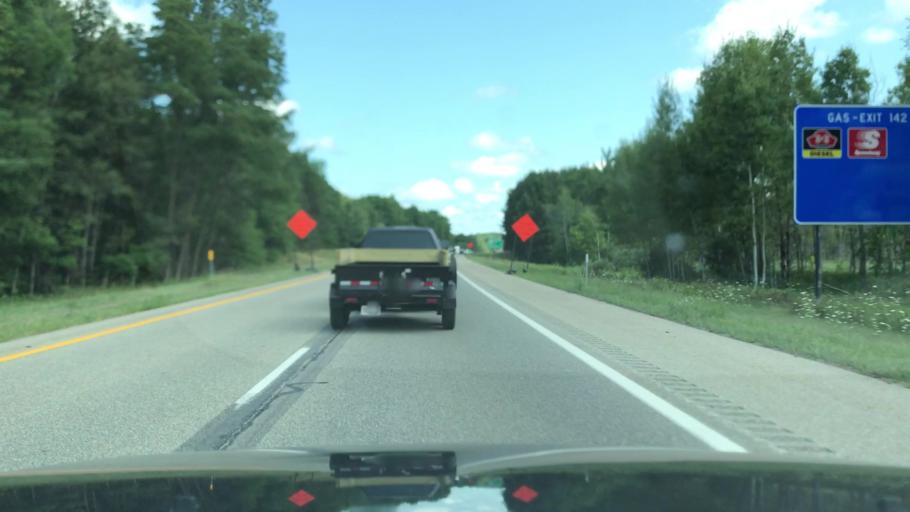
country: US
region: Michigan
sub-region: Mecosta County
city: Big Rapids
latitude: 43.7319
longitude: -85.5328
